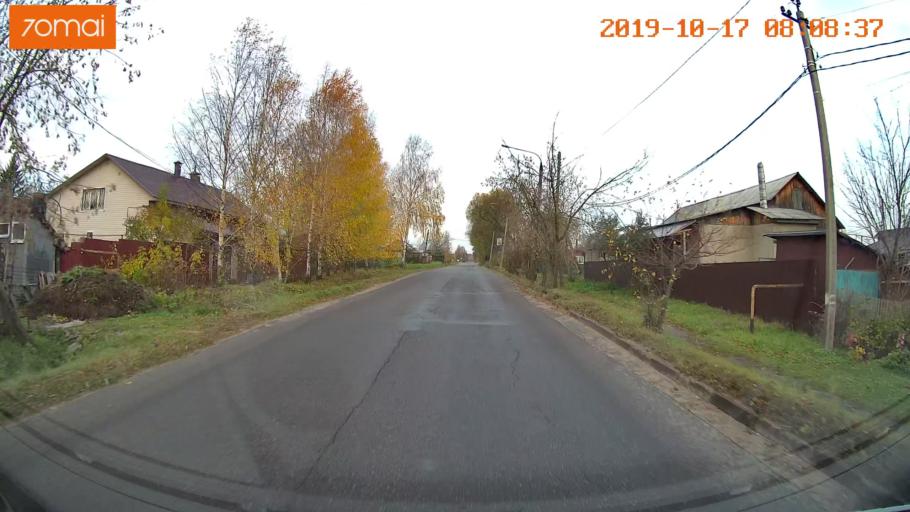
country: RU
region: Vladimir
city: Kol'chugino
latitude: 56.3146
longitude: 39.3858
